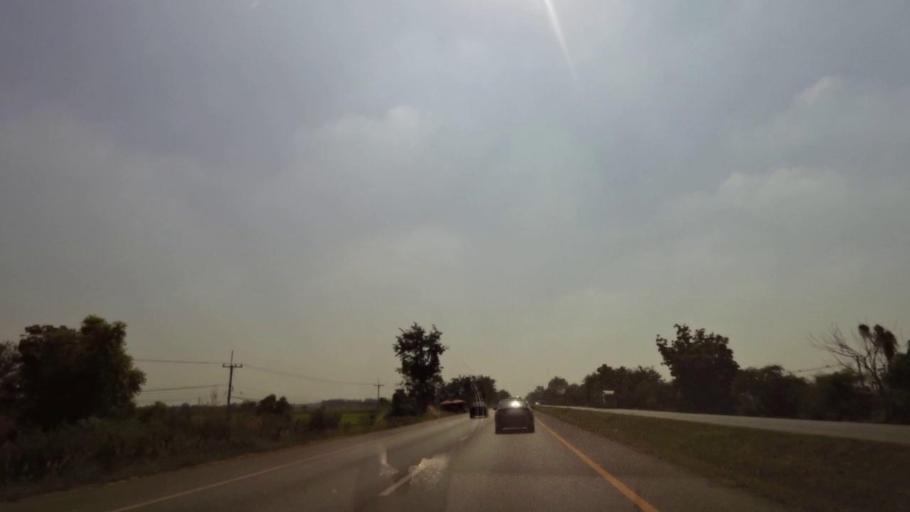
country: TH
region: Phichit
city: Wachira Barami
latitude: 16.4491
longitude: 100.1464
